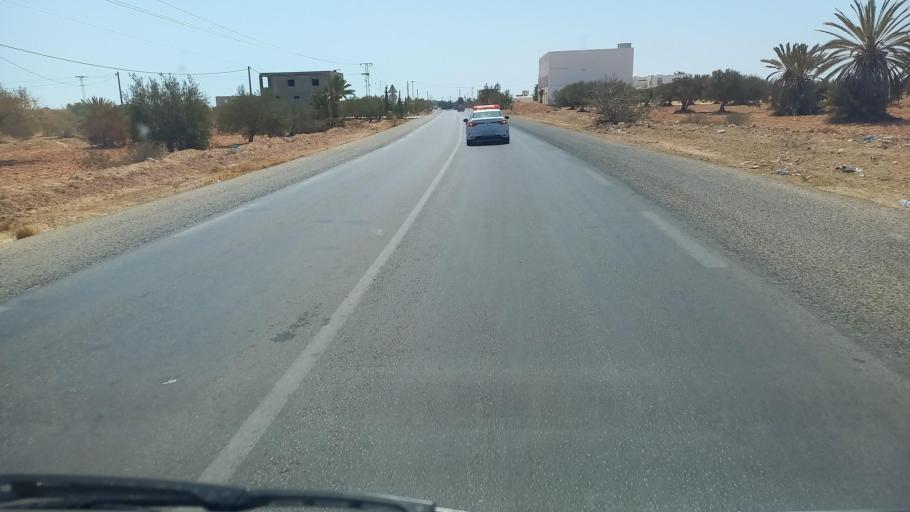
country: TN
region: Madanin
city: Houmt Souk
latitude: 33.8182
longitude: 10.8723
